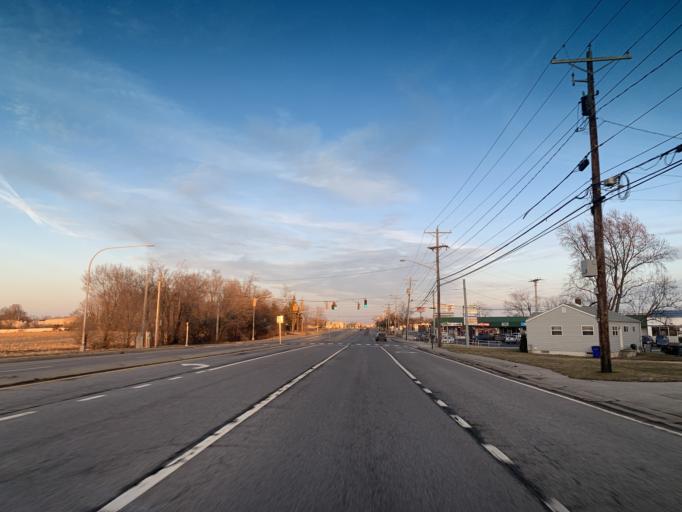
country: US
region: Delaware
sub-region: New Castle County
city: Wilmington Manor
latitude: 39.6646
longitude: -75.6186
